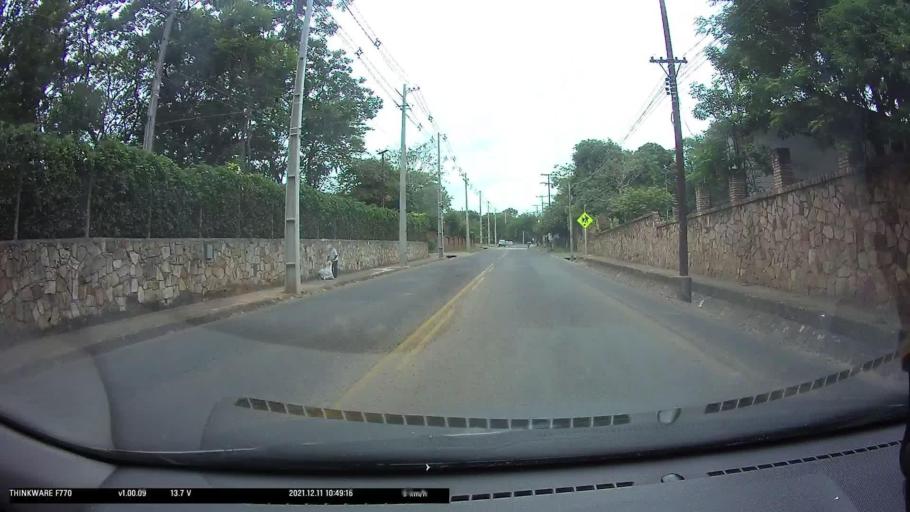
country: PY
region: Cordillera
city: San Bernardino
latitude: -25.2967
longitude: -57.2821
